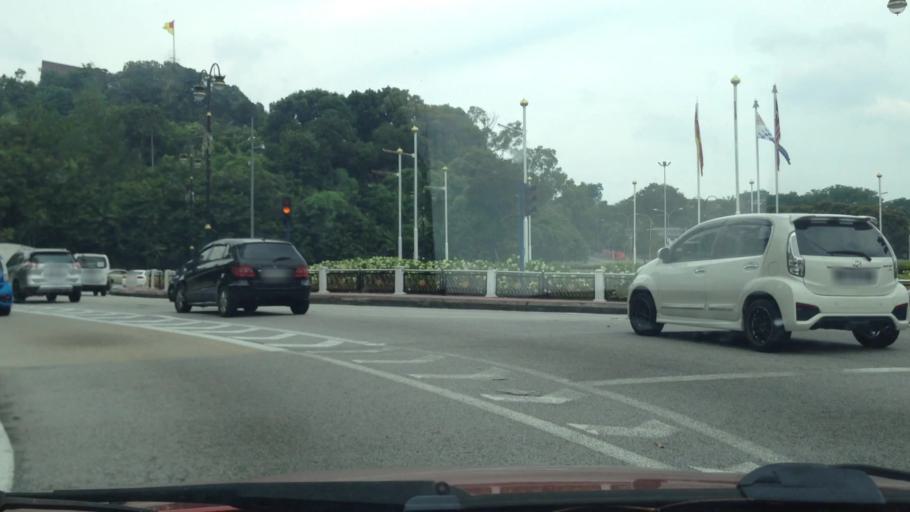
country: MY
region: Selangor
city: Shah Alam
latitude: 3.0749
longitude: 101.5336
